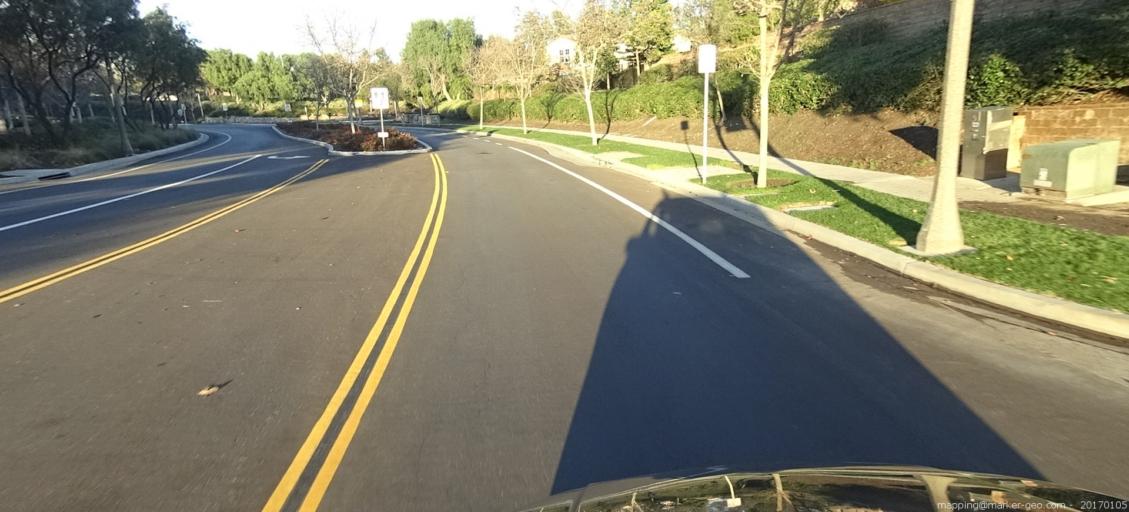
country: US
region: California
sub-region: Orange County
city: Ladera Ranch
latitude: 33.5404
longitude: -117.6407
